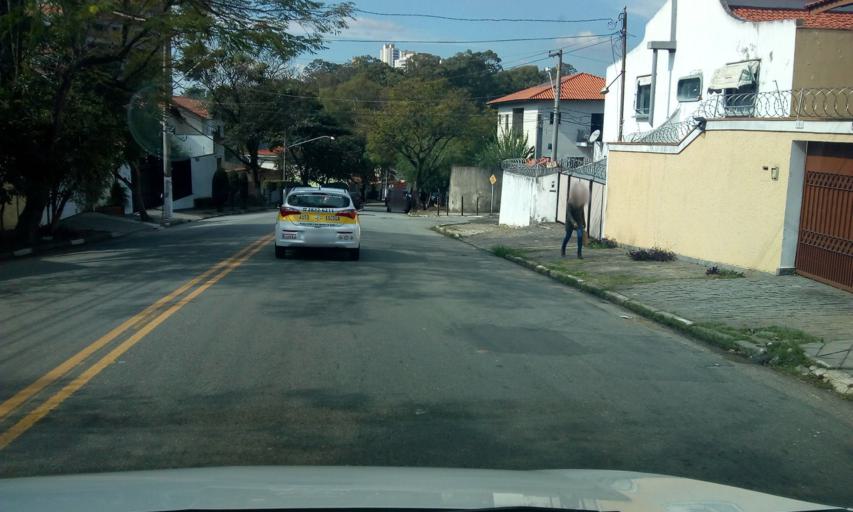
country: BR
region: Sao Paulo
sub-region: Osasco
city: Osasco
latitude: -23.5592
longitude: -46.7688
